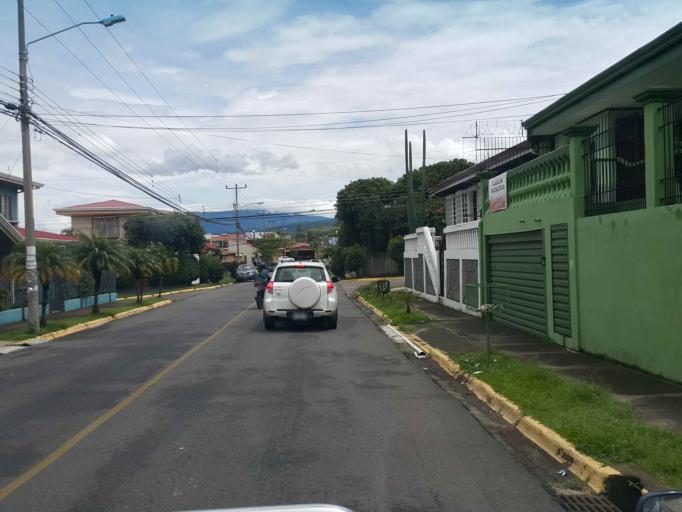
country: CR
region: Heredia
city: Heredia
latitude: 10.0172
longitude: -84.1181
